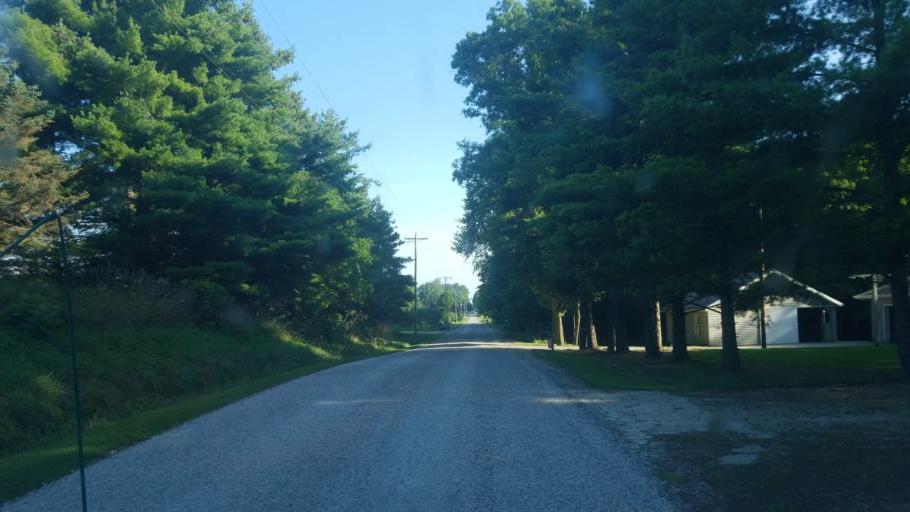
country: US
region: Ohio
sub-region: Ashland County
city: Ashland
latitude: 40.9362
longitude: -82.3398
